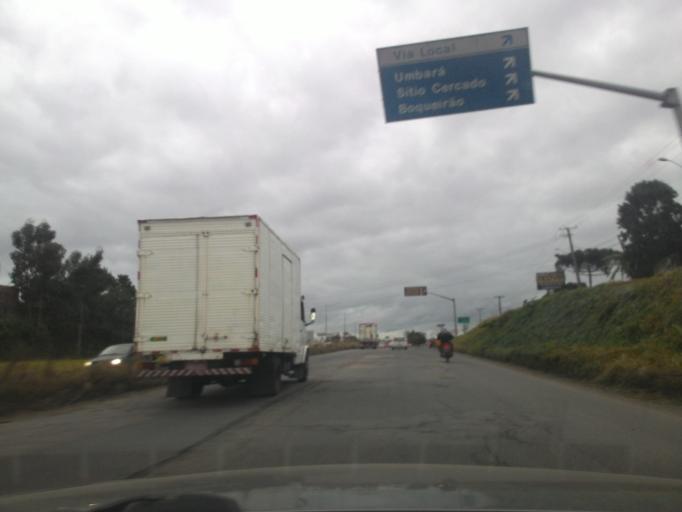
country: BR
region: Parana
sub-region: Sao Jose Dos Pinhais
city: Sao Jose dos Pinhais
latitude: -25.5314
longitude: -49.2997
